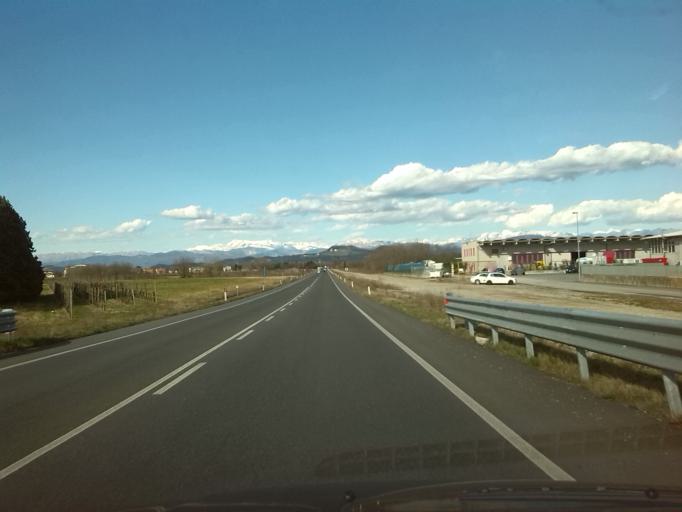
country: IT
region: Friuli Venezia Giulia
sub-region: Provincia di Gorizia
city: Mariano del Friuli
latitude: 45.9060
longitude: 13.4671
